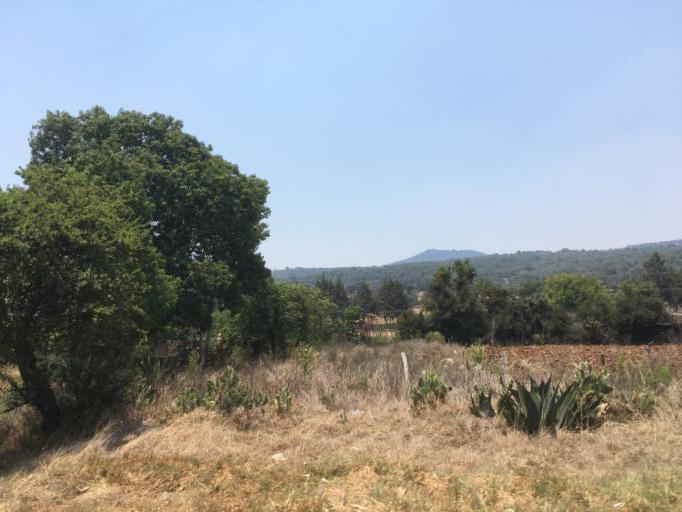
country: MX
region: Michoacan
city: Quiroga
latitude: 19.6358
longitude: -101.4734
